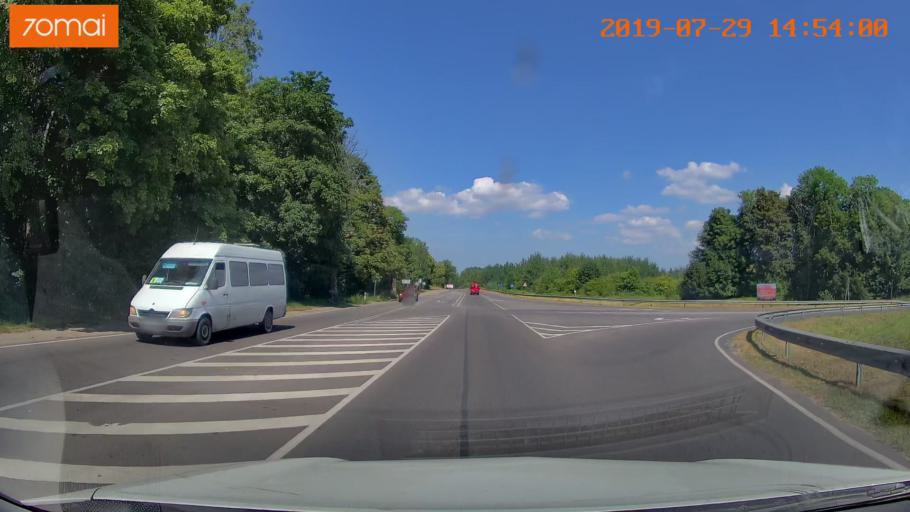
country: RU
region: Kaliningrad
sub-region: Gorod Kaliningrad
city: Baltiysk
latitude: 54.6703
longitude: 19.9216
